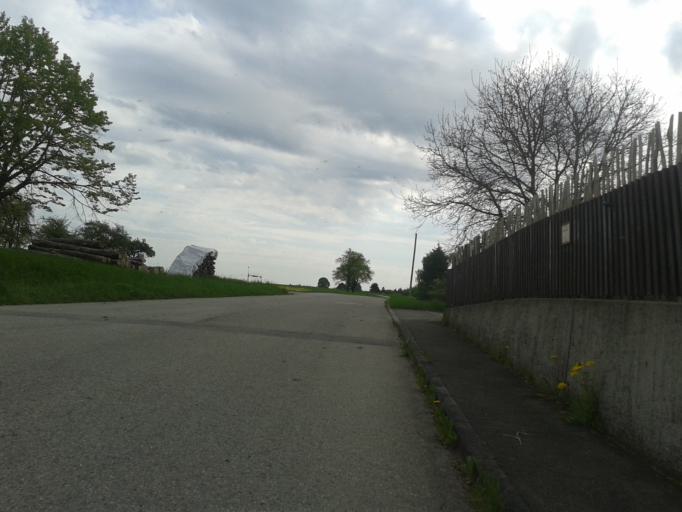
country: DE
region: Baden-Wuerttemberg
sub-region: Tuebingen Region
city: Blaubeuren
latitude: 48.3795
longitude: 9.8110
